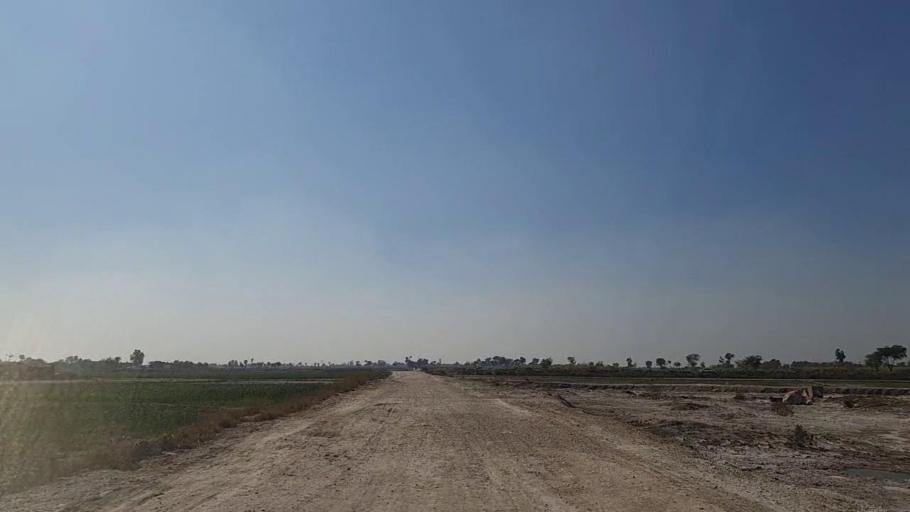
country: PK
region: Sindh
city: Bandhi
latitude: 26.5315
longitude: 68.3044
